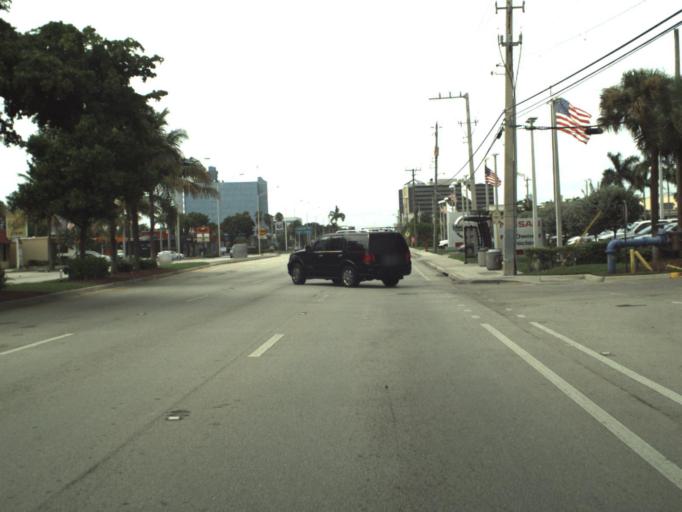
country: US
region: Florida
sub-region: Broward County
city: Terra Mar
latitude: 26.2147
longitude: -80.1062
